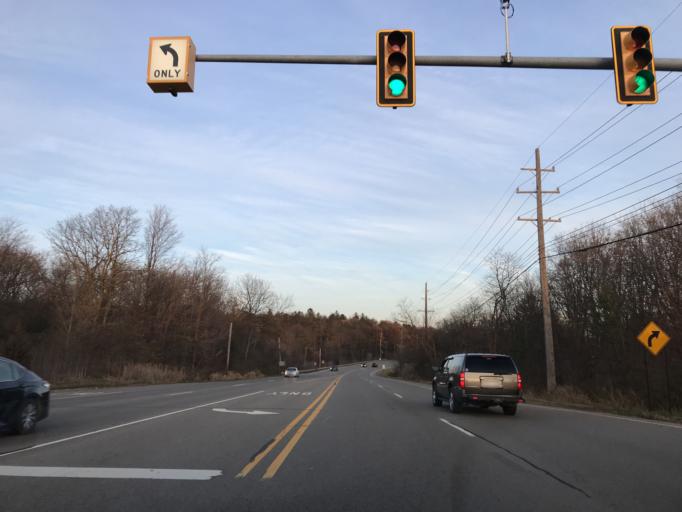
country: US
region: Michigan
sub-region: Washtenaw County
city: Ann Arbor
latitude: 42.3108
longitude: -83.6725
